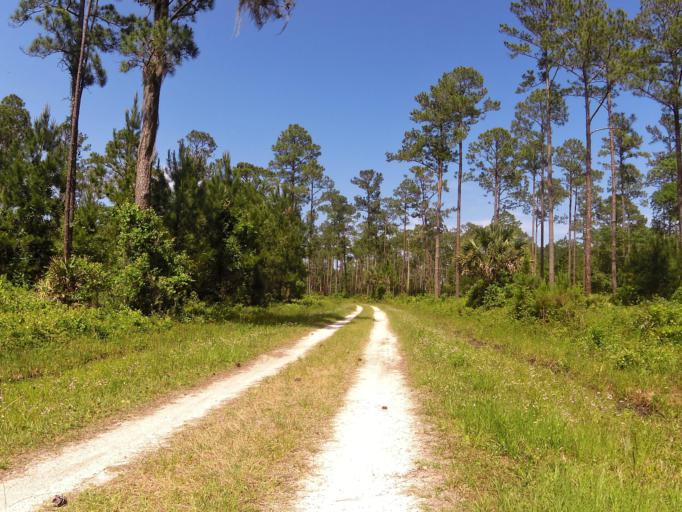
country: US
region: Florida
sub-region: Saint Johns County
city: Palm Valley
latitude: 30.1394
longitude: -81.3769
